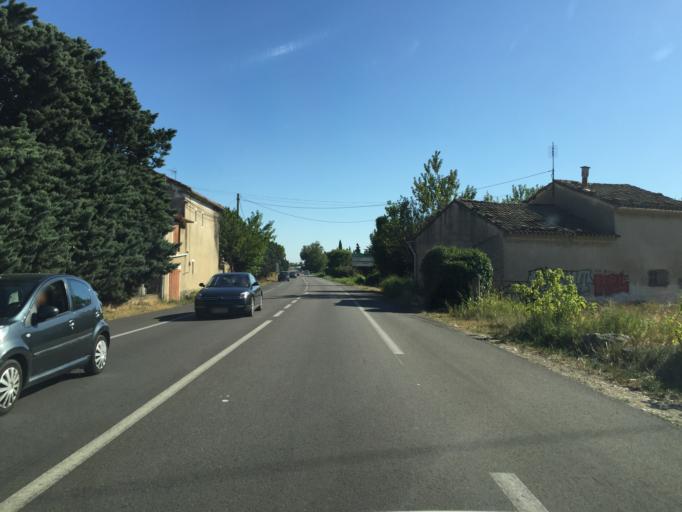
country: FR
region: Provence-Alpes-Cote d'Azur
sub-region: Departement du Vaucluse
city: Carpentras
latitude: 44.0318
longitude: 5.0385
